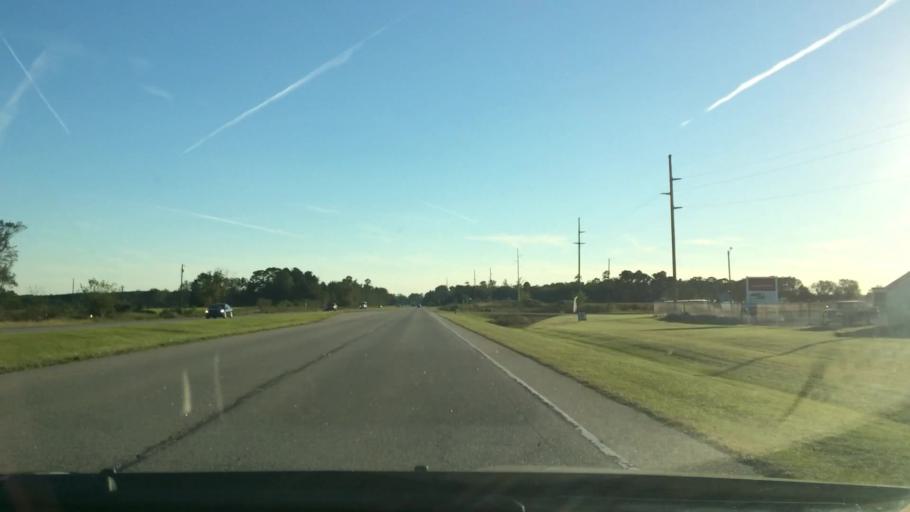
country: US
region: North Carolina
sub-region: Pitt County
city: Grifton
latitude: 35.3755
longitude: -77.4532
